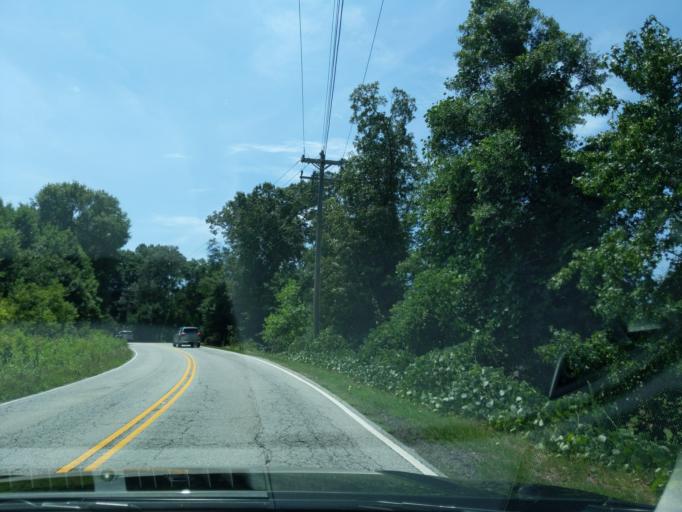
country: US
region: South Carolina
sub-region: Greenville County
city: Five Forks
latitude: 34.7690
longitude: -82.2079
